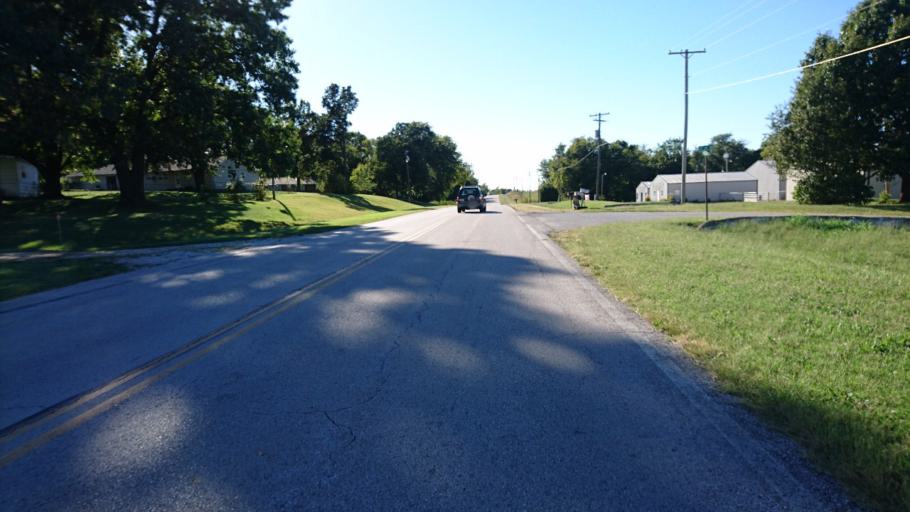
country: US
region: Missouri
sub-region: Jasper County
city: Carthage
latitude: 37.1732
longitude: -94.3567
